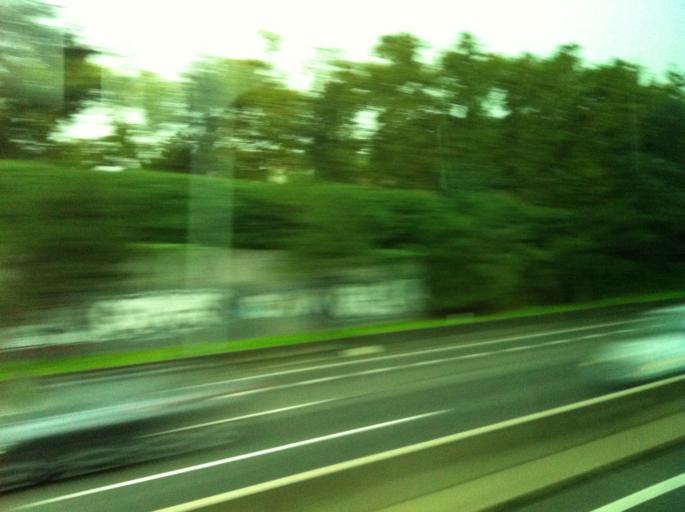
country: ES
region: Madrid
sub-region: Provincia de Madrid
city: Moncloa-Aravaca
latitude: 40.4612
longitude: -3.7631
